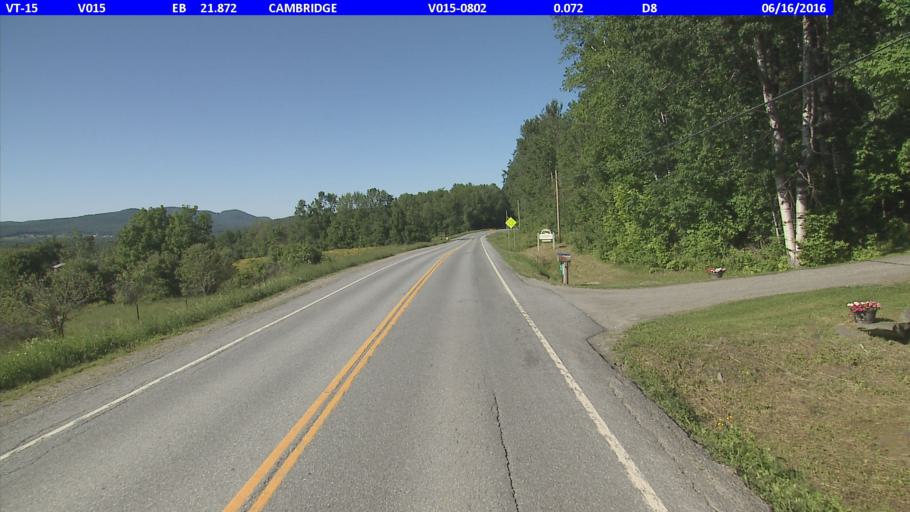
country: US
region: Vermont
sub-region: Chittenden County
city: Jericho
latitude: 44.6329
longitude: -72.9153
